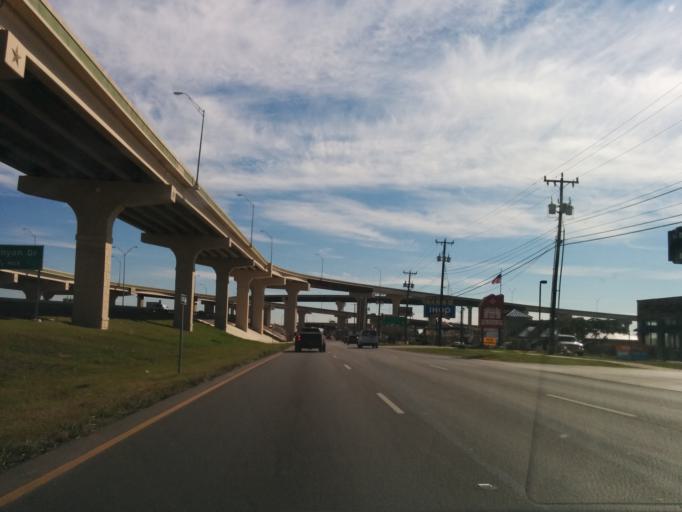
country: US
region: Texas
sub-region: Bexar County
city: Hollywood Park
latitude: 29.6096
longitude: -98.4722
